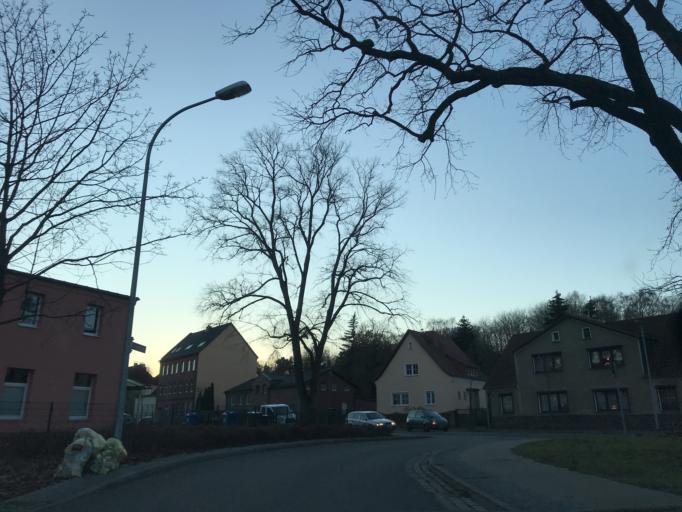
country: DE
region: Brandenburg
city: Rathenow
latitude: 52.5996
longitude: 12.3375
